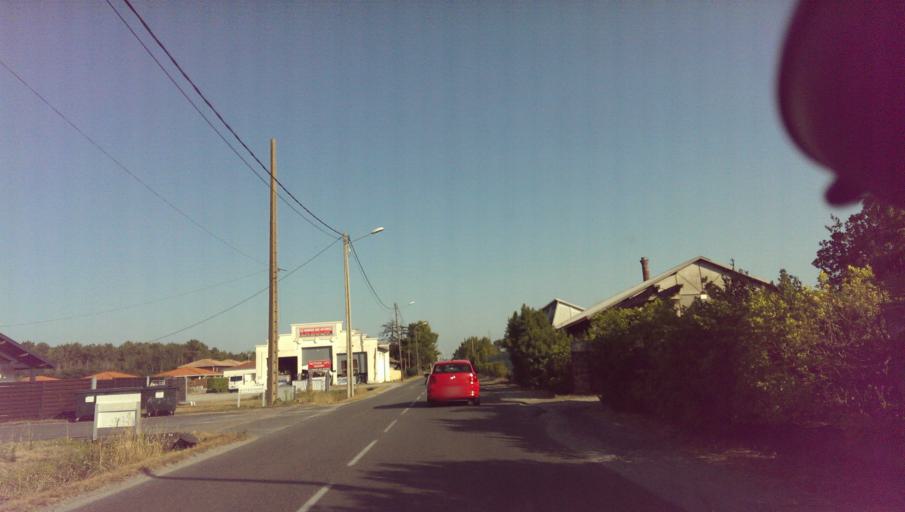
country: FR
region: Aquitaine
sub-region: Departement des Landes
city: Mimizan
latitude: 44.1971
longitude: -1.2237
